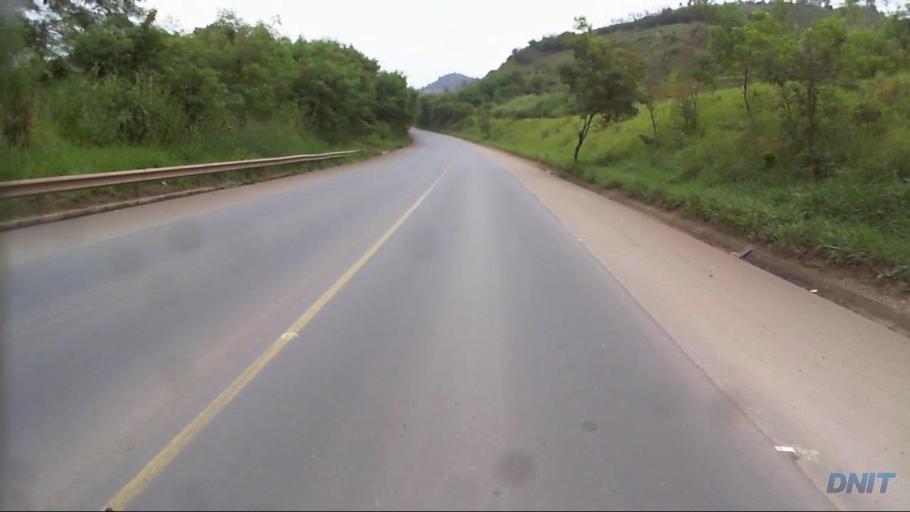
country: BR
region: Minas Gerais
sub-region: Coronel Fabriciano
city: Coronel Fabriciano
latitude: -19.5242
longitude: -42.6580
